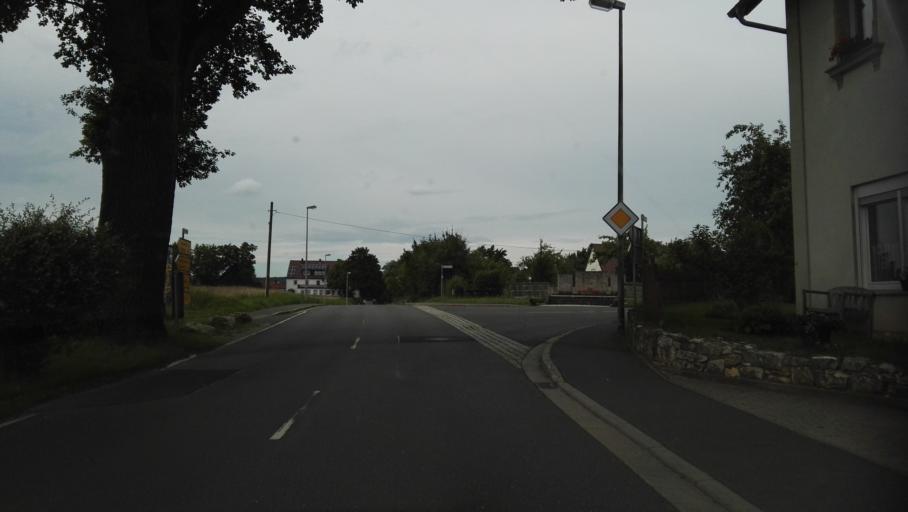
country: DE
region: Bavaria
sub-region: Upper Franconia
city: Plankenfels
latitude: 49.8855
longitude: 11.3344
